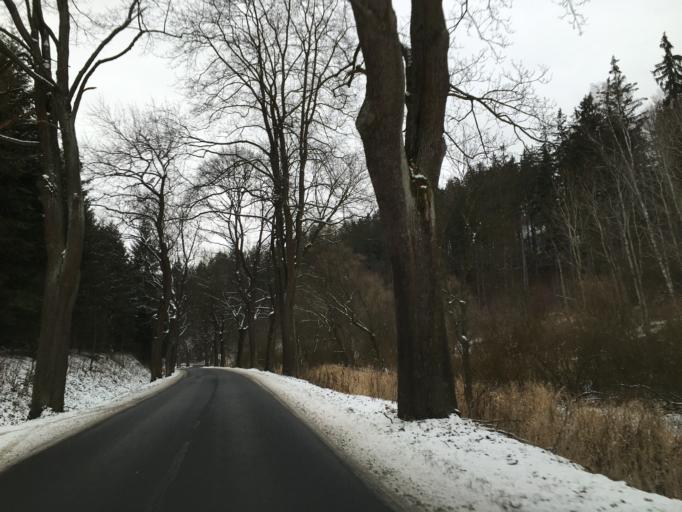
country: PL
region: Lower Silesian Voivodeship
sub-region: Powiat kamiennogorski
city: Krzeszow
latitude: 50.7027
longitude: 16.1294
